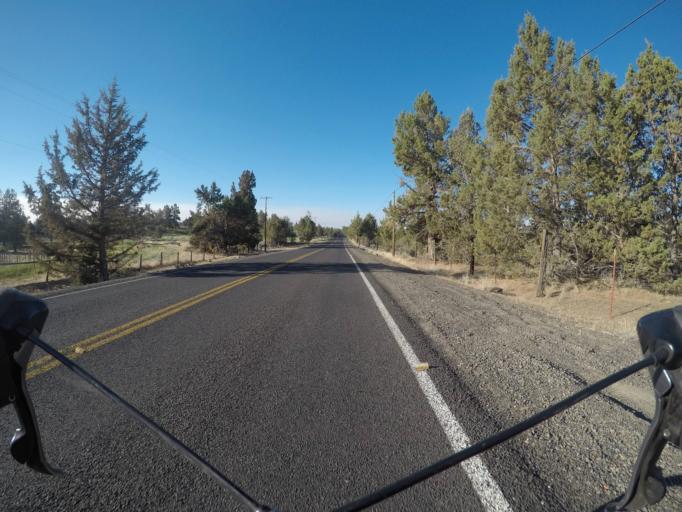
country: US
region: Oregon
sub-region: Deschutes County
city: Redmond
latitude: 44.2538
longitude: -121.2396
